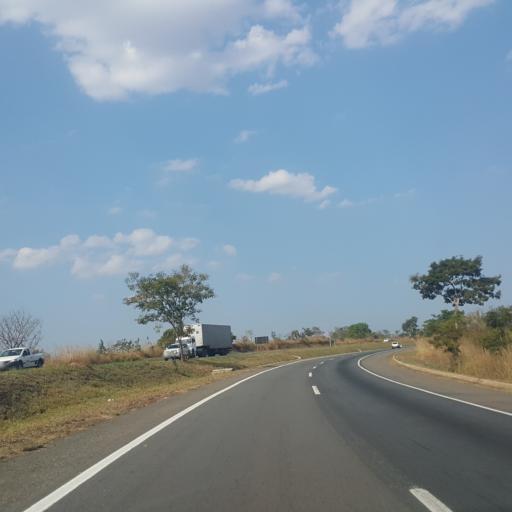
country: BR
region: Goias
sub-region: Abadiania
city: Abadiania
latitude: -16.1139
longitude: -48.5447
